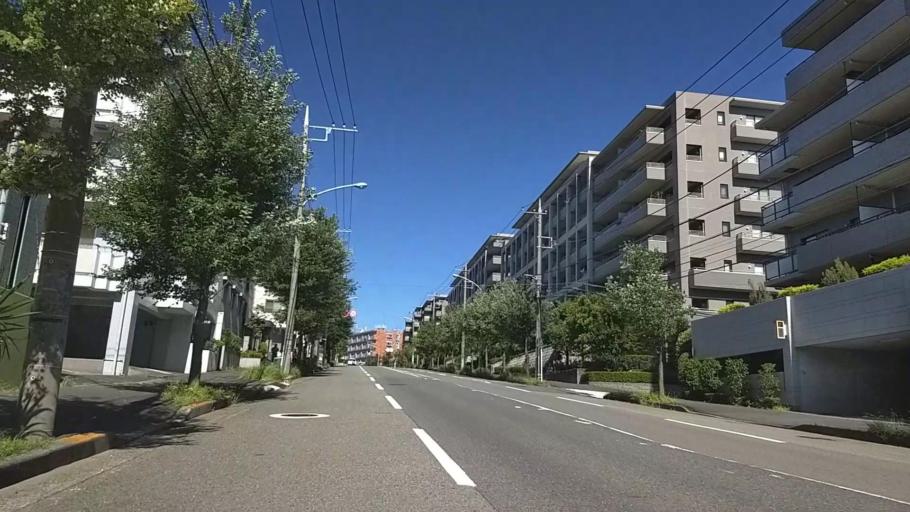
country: JP
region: Tokyo
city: Chofugaoka
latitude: 35.5695
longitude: 139.5591
